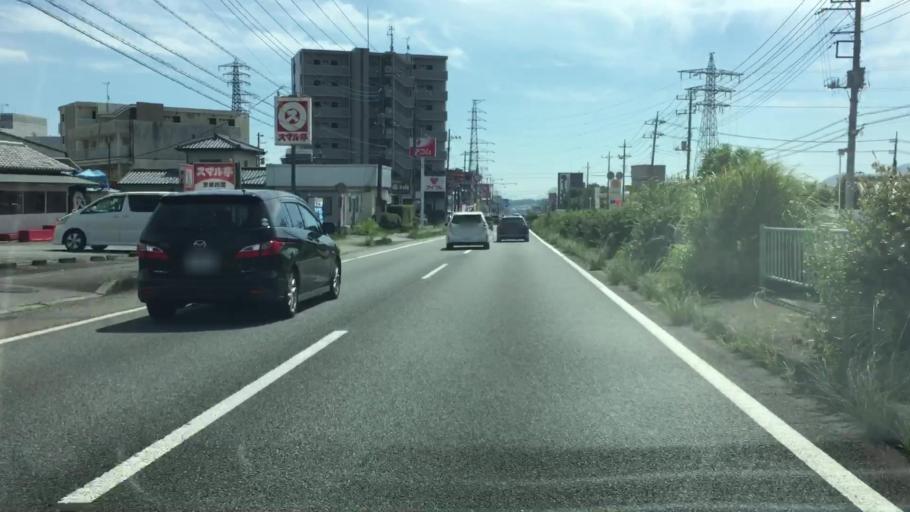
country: JP
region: Shizuoka
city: Fujinomiya
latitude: 35.2438
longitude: 138.6184
